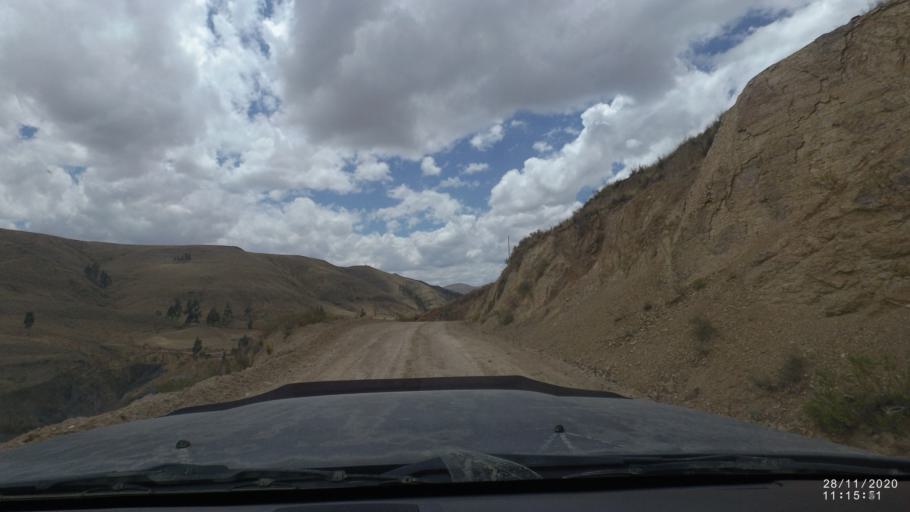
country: BO
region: Cochabamba
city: Tarata
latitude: -17.7463
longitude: -66.0866
